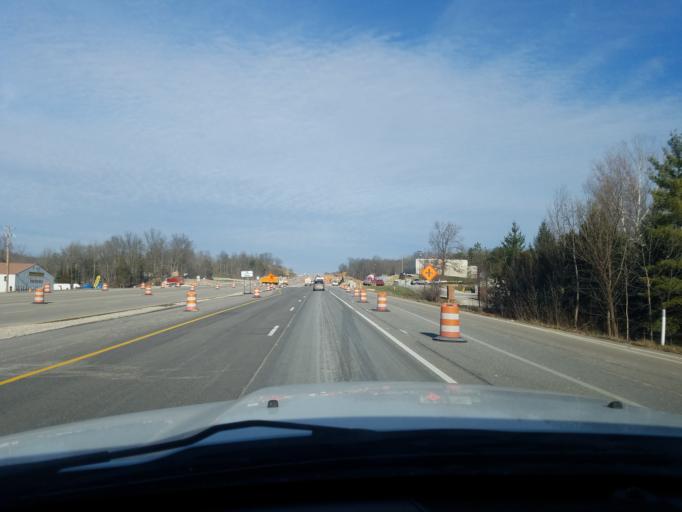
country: US
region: Indiana
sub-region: Monroe County
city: Bloomington
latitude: 39.2433
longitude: -86.5346
